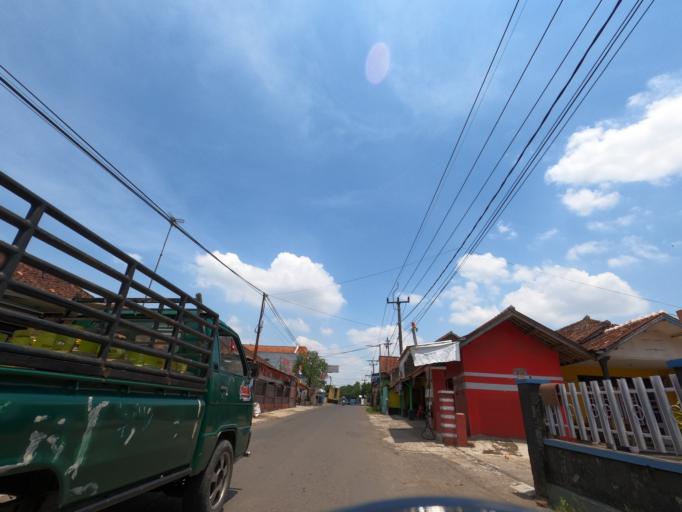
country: ID
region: West Java
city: Pamanukan
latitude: -6.5383
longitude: 107.7695
